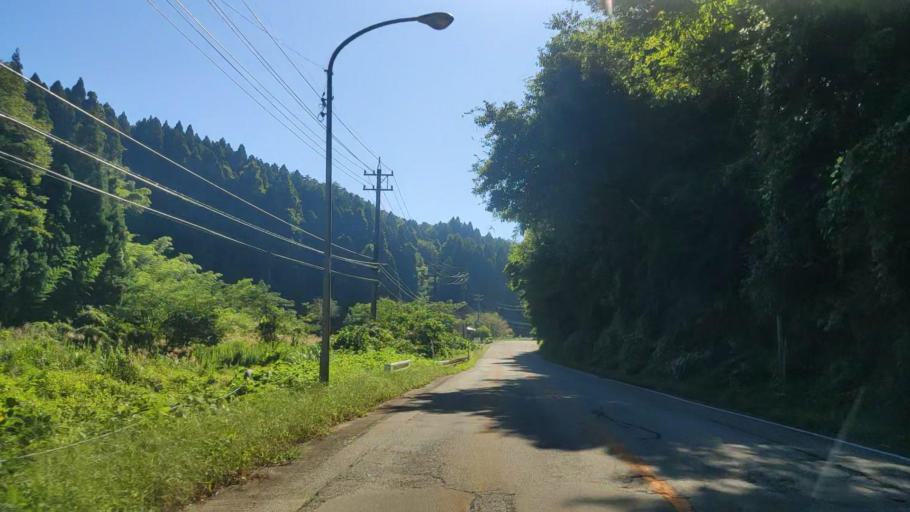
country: JP
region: Ishikawa
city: Nanao
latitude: 37.3227
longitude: 137.1902
